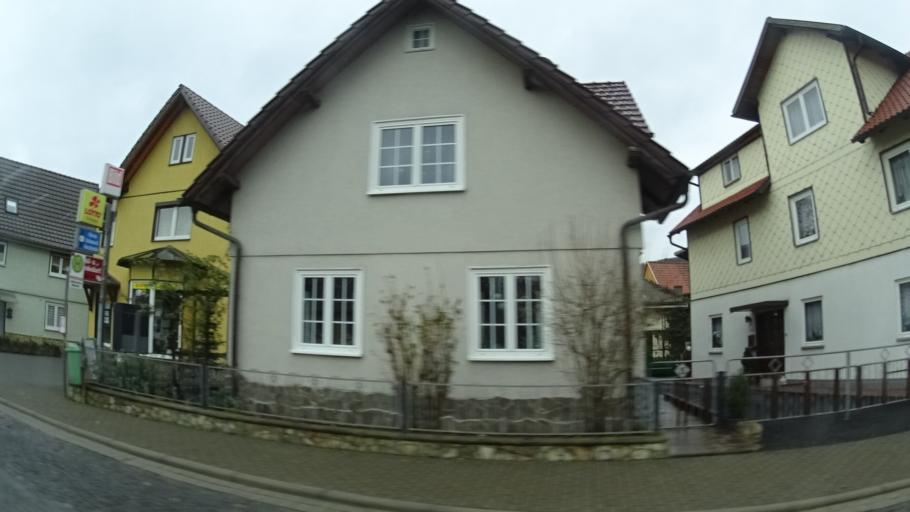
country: DE
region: Thuringia
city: Juchsen
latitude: 50.4807
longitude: 10.5022
